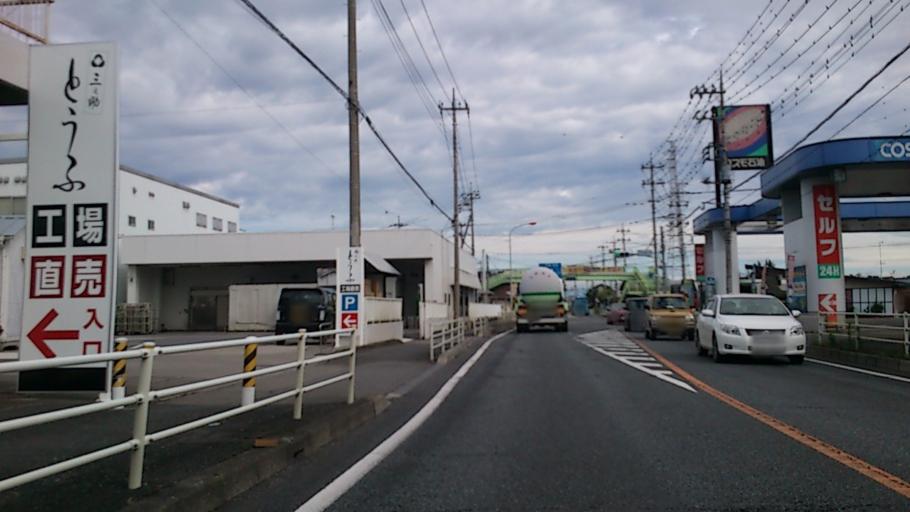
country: JP
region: Saitama
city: Honjo
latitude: 36.2358
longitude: 139.2080
